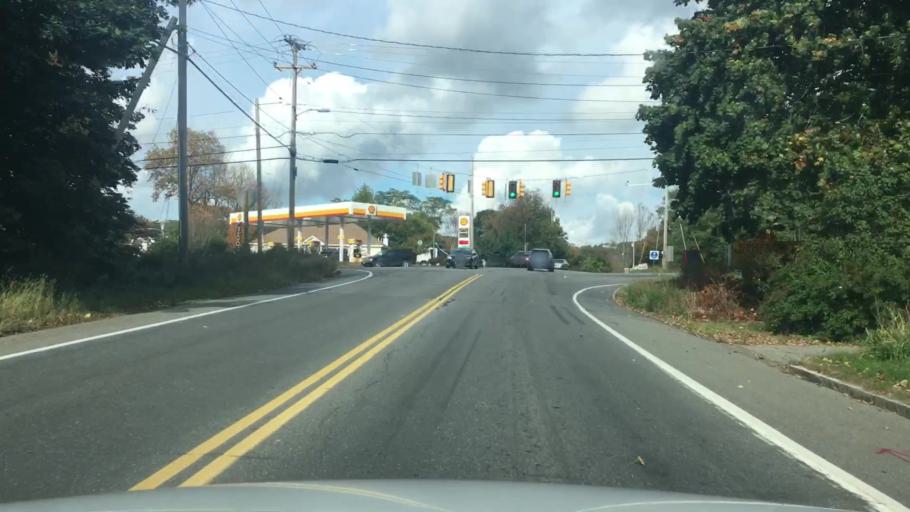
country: US
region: Maine
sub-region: Knox County
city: Rockland
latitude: 44.1232
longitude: -69.1169
